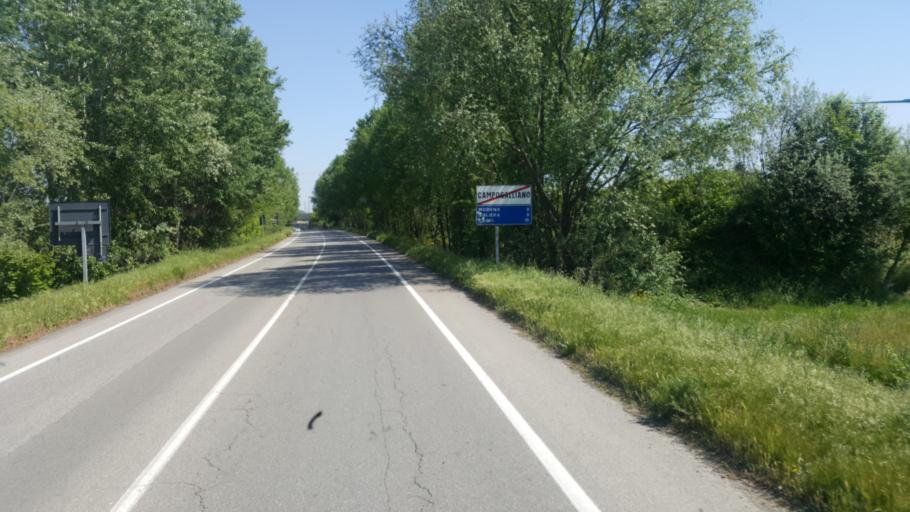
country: IT
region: Emilia-Romagna
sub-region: Provincia di Modena
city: Campogalliano
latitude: 44.6828
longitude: 10.8610
